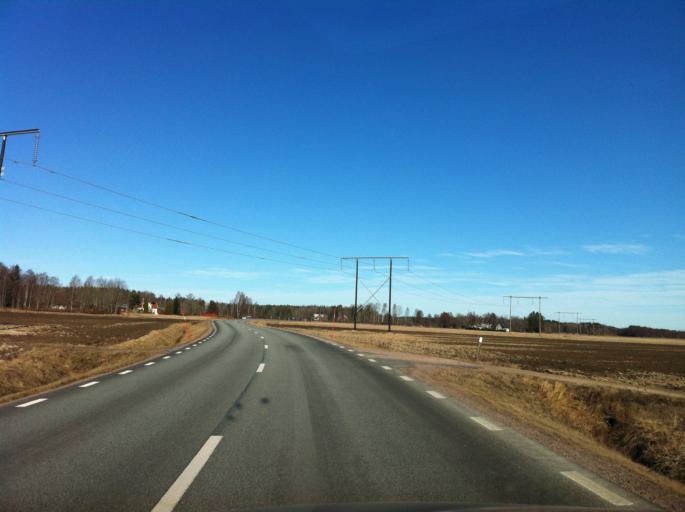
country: SE
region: Vaestra Goetaland
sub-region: Toreboda Kommun
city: Toereboda
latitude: 58.6815
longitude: 14.1063
